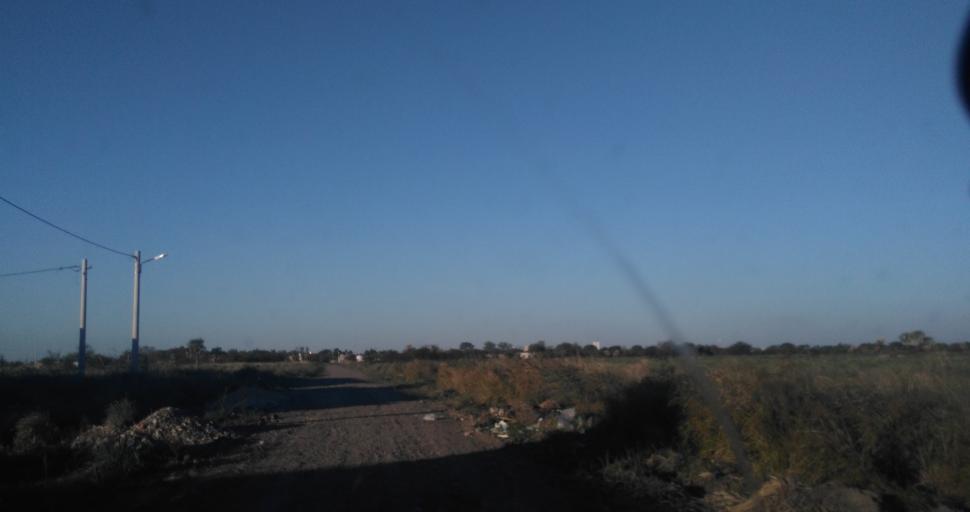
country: AR
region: Chaco
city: Resistencia
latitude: -27.4753
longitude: -59.0258
